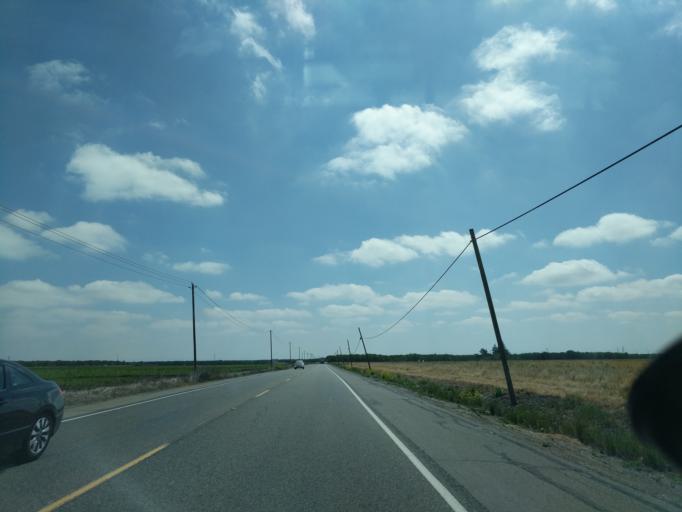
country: US
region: California
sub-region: San Joaquin County
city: Garden Acres
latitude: 37.9489
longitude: -121.1734
